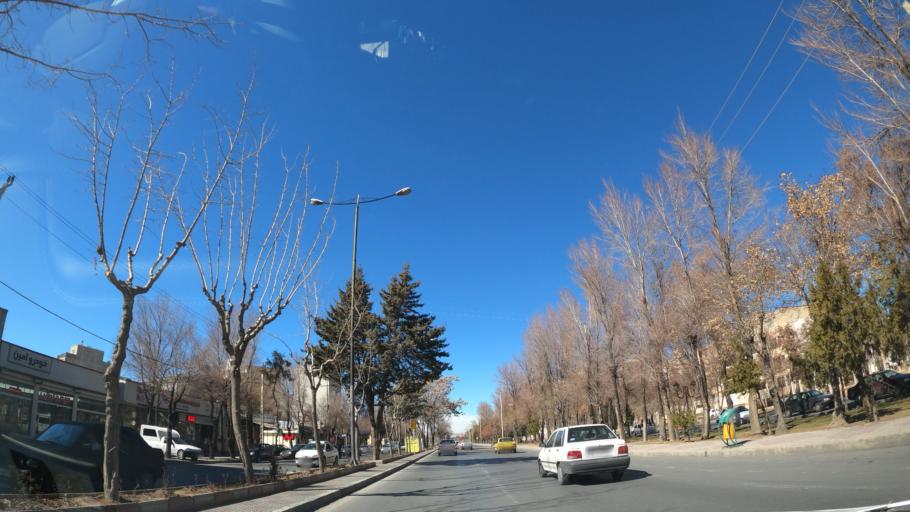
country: IR
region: Chahar Mahall va Bakhtiari
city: Shahrekord
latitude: 32.3130
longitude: 50.8793
